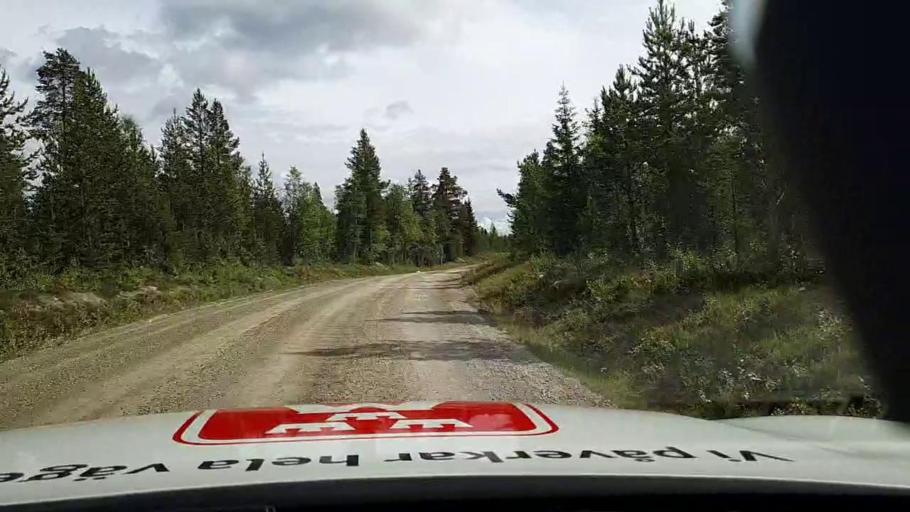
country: SE
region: Jaemtland
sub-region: Are Kommun
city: Jarpen
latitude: 62.5391
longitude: 13.4748
